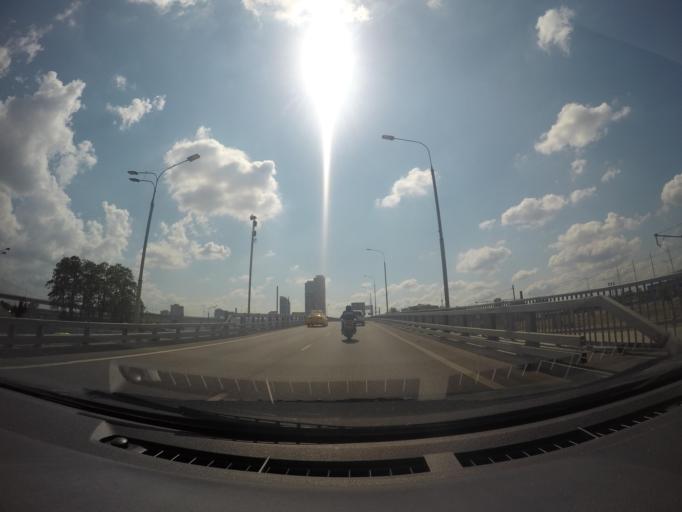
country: RU
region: Moscow
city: Rostokino
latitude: 55.8432
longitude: 37.6661
